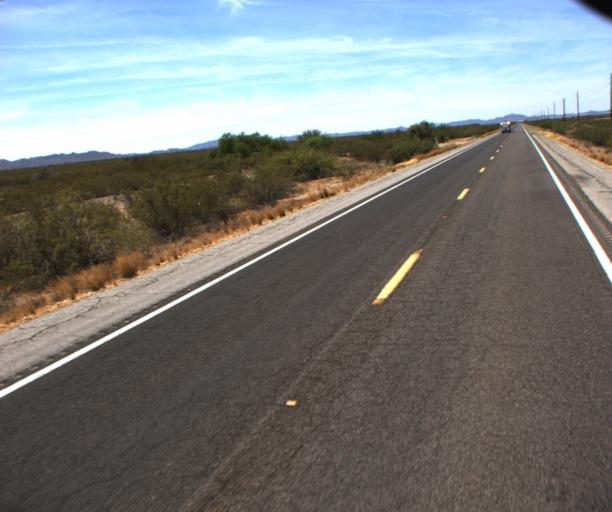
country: US
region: Arizona
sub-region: La Paz County
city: Salome
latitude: 33.8437
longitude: -113.4698
